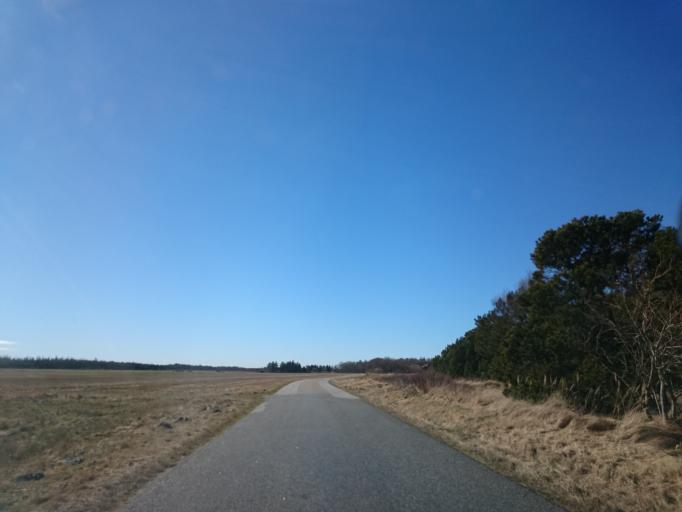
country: DK
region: North Denmark
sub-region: Frederikshavn Kommune
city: Strandby
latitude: 57.6258
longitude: 10.3698
